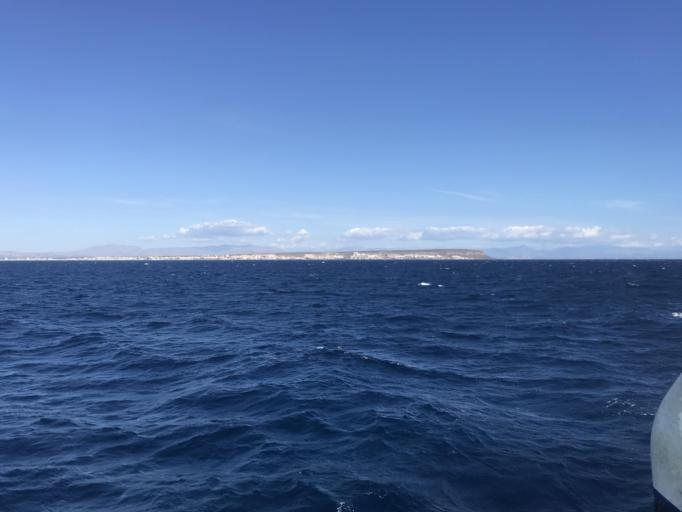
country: ES
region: Valencia
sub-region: Provincia de Alicante
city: Santa Pola
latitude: 38.1356
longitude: -0.5304
